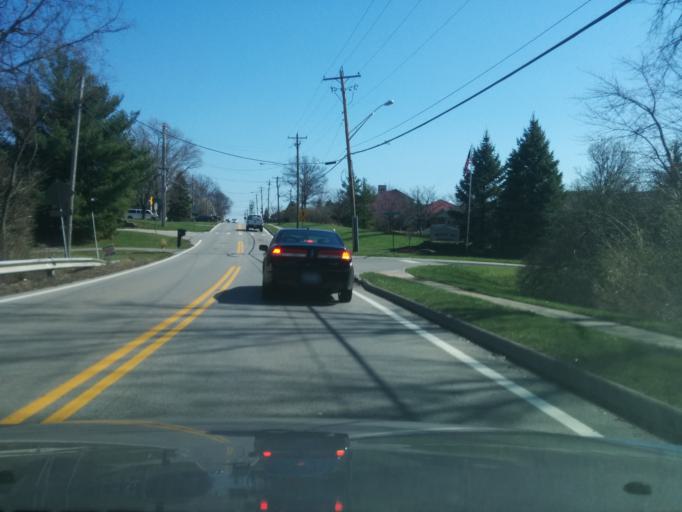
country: US
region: Ohio
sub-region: Hamilton County
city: Monfort Heights
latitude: 39.1895
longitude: -84.6109
